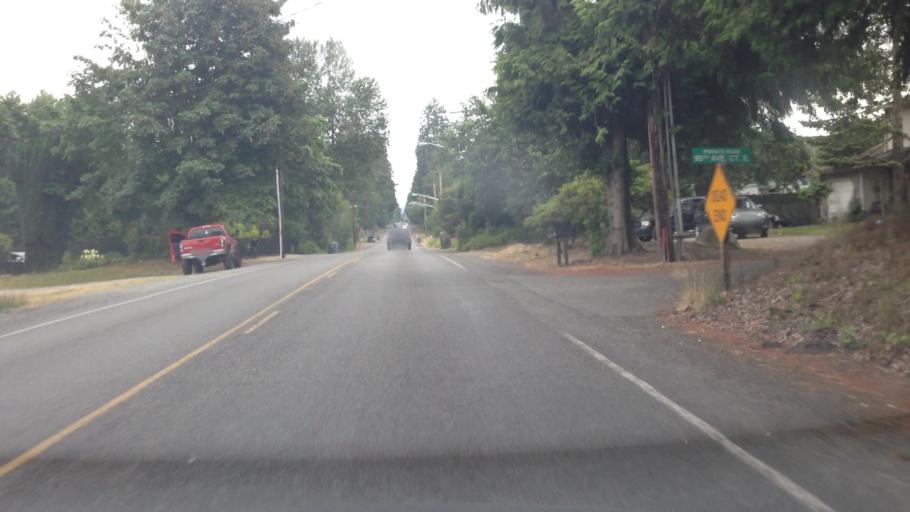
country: US
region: Washington
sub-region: Pierce County
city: South Hill
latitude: 47.1184
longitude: -122.3028
